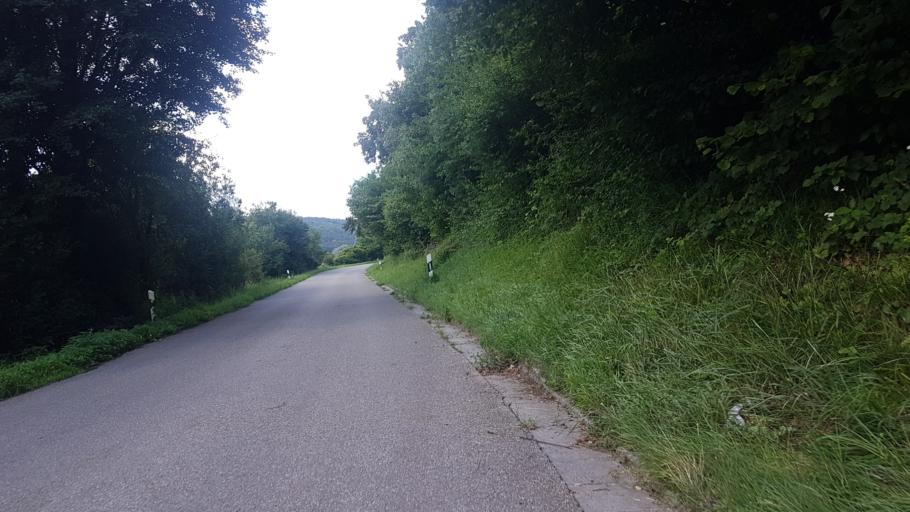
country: DE
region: Bavaria
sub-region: Upper Bavaria
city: Walting
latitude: 48.8932
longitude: 11.2634
